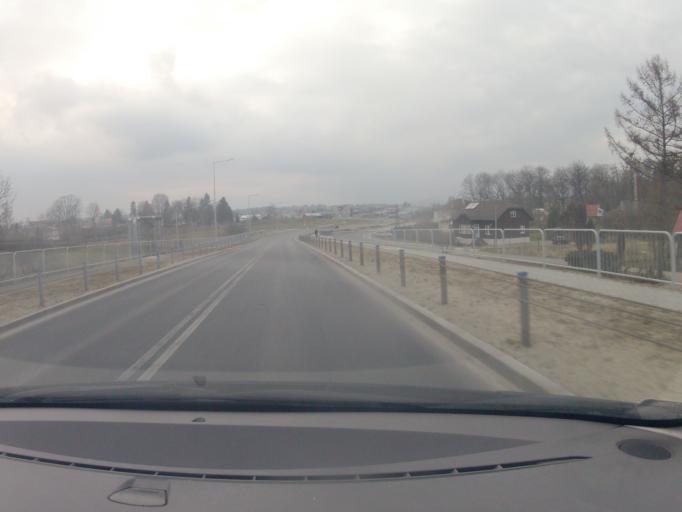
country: PL
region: Subcarpathian Voivodeship
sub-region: Powiat jasielski
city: Jaslo
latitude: 49.7498
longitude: 21.4807
